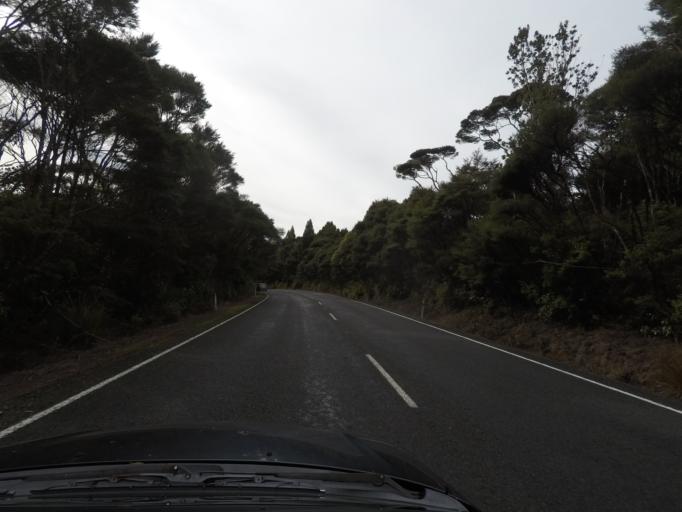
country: NZ
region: Auckland
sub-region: Auckland
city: Titirangi
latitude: -36.9404
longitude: 174.5540
